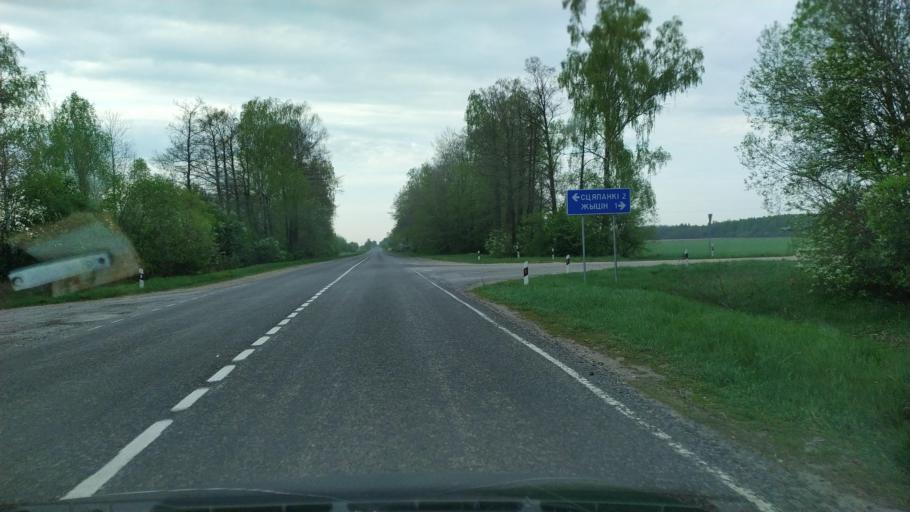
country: BY
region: Brest
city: Zhabinka
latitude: 52.2661
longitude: 23.9590
